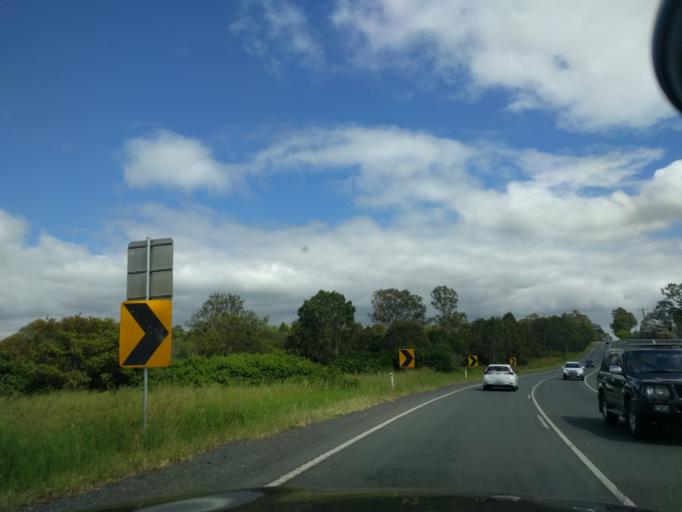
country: AU
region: Queensland
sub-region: Logan
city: Cedar Vale
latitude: -27.9059
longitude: 152.9762
